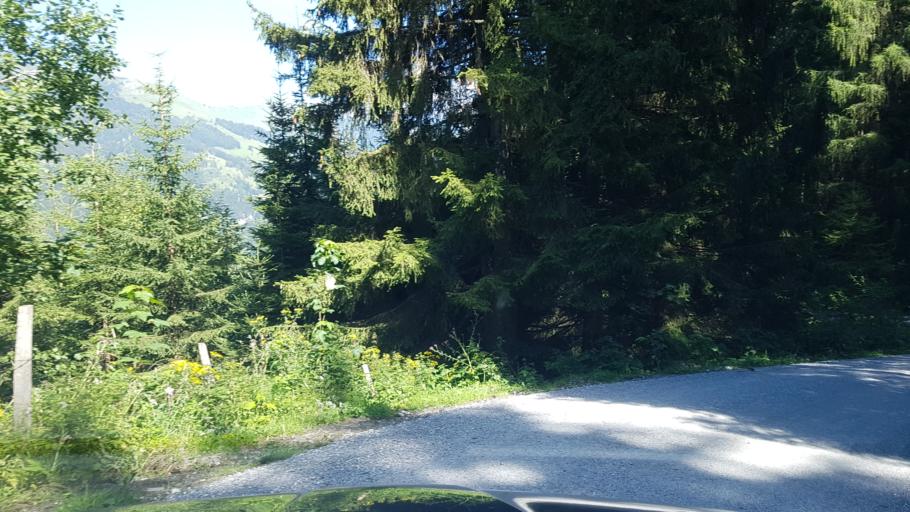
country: AT
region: Salzburg
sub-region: Politischer Bezirk Sankt Johann im Pongau
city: Dorfgastein
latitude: 47.2532
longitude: 13.0722
